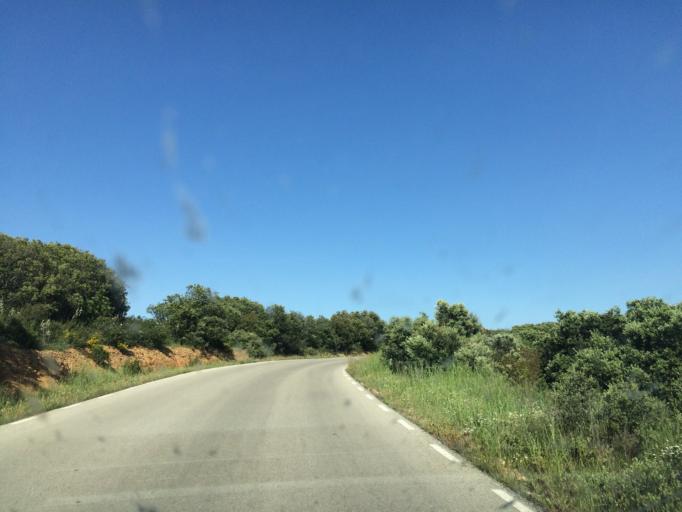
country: ES
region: Madrid
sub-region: Provincia de Madrid
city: Valdepielagos
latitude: 40.7558
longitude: -3.4141
